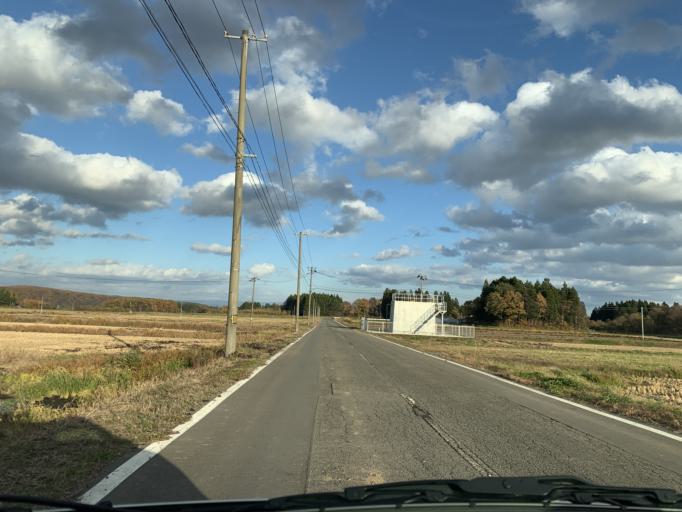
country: JP
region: Iwate
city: Mizusawa
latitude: 39.1187
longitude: 140.9792
